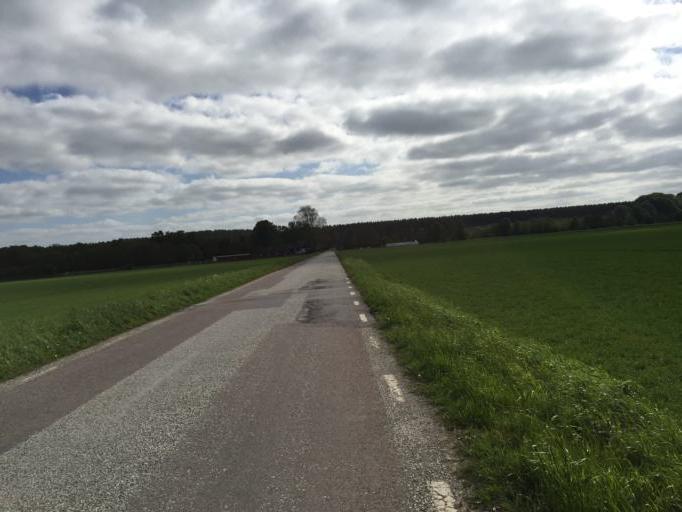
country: SE
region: Skane
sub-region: Sjobo Kommun
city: Blentarp
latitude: 55.6659
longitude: 13.6209
